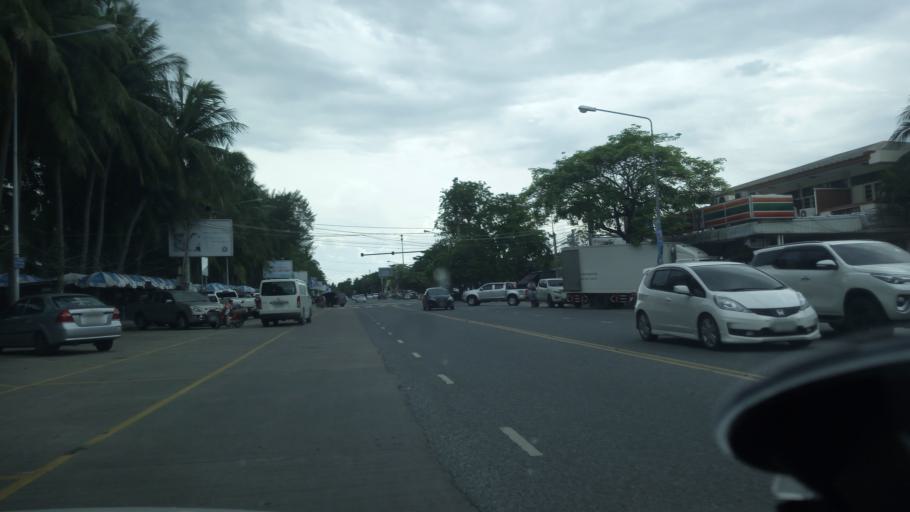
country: TH
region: Chon Buri
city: Chon Buri
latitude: 13.2895
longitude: 100.9108
